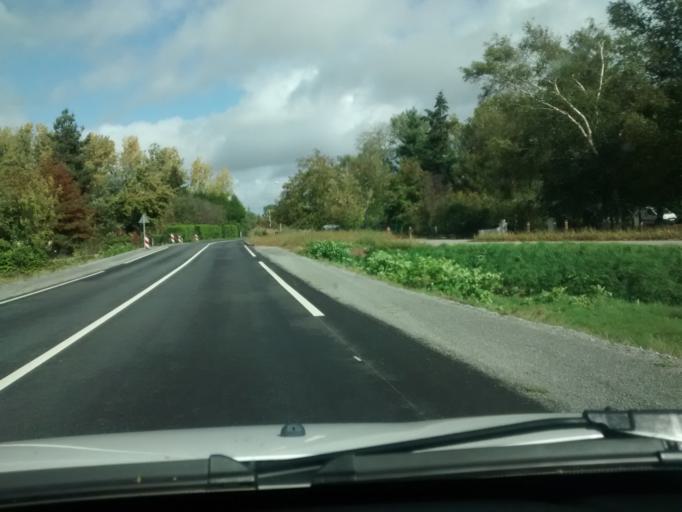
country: FR
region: Brittany
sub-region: Departement d'Ille-et-Vilaine
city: Servon-sur-Vilaine
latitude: 48.1156
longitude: -1.4660
